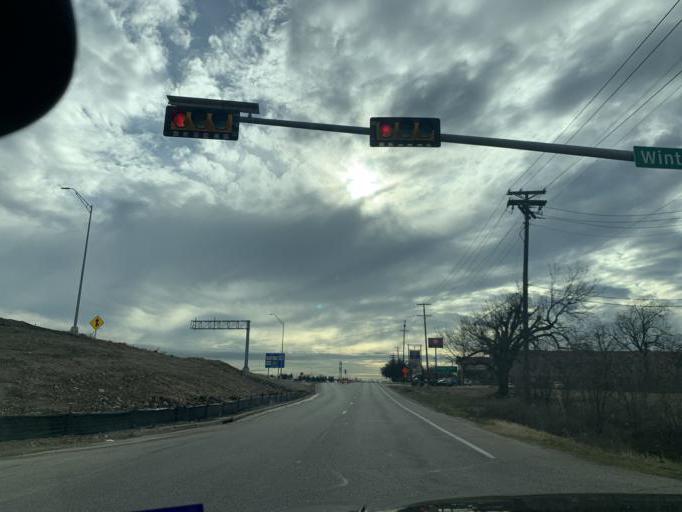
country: US
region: Texas
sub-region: Dallas County
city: Duncanville
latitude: 32.6188
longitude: -96.9157
